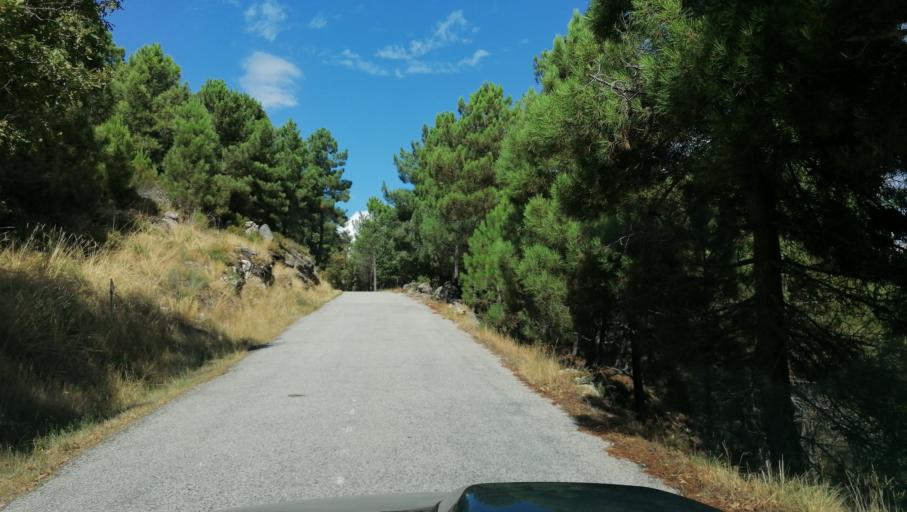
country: PT
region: Vila Real
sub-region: Vila Pouca de Aguiar
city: Vila Pouca de Aguiar
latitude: 41.5559
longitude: -7.6559
